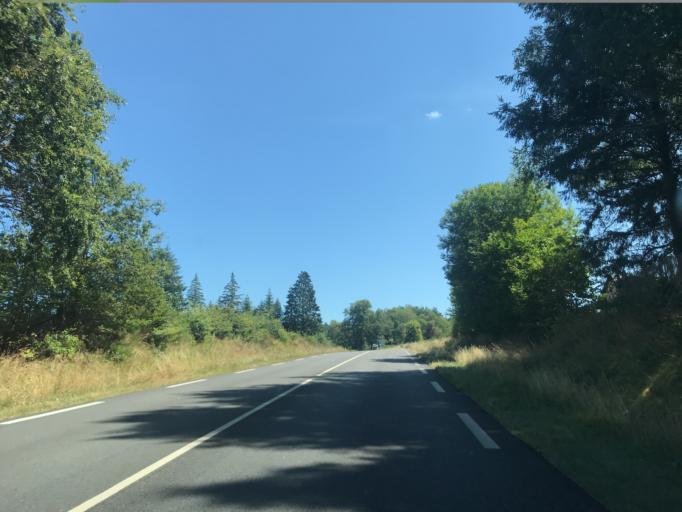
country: FR
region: Limousin
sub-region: Departement de la Correze
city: Correze
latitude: 45.3456
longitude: 1.9440
